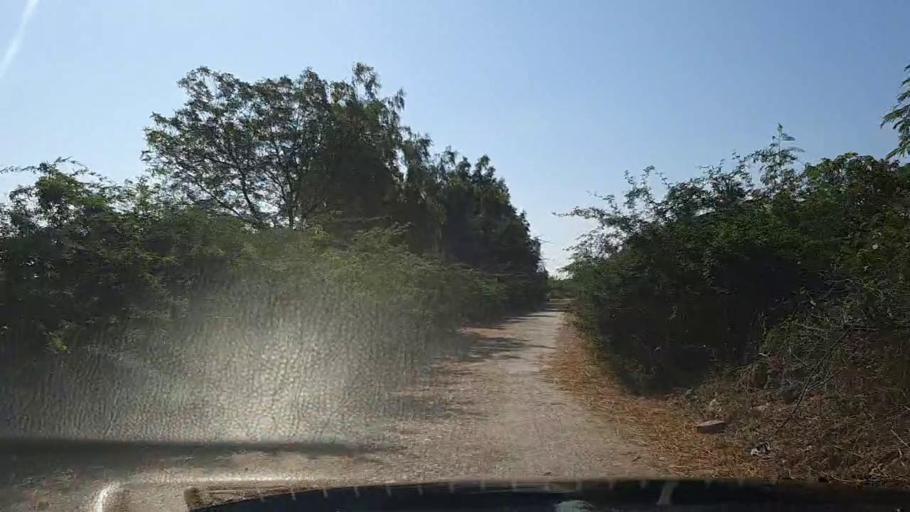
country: PK
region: Sindh
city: Thatta
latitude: 24.7108
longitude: 67.9188
